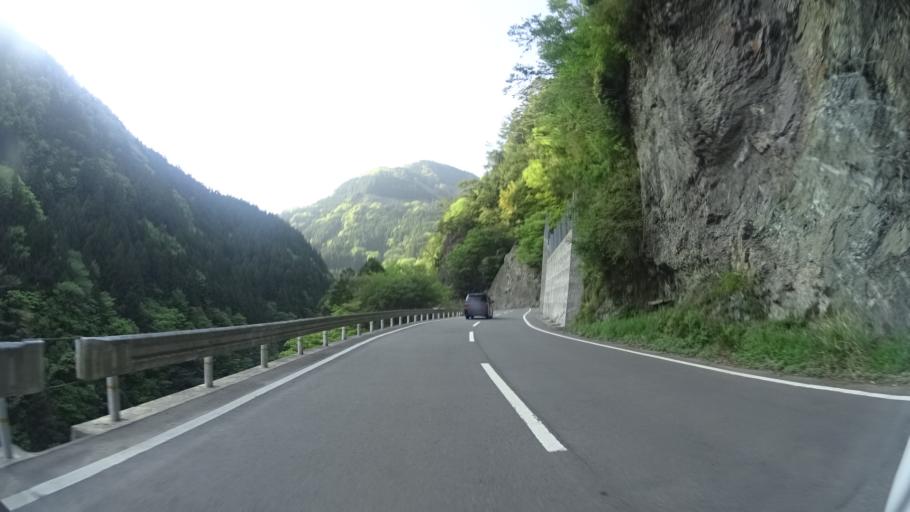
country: JP
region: Tokushima
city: Ikedacho
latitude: 33.8761
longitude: 133.8693
